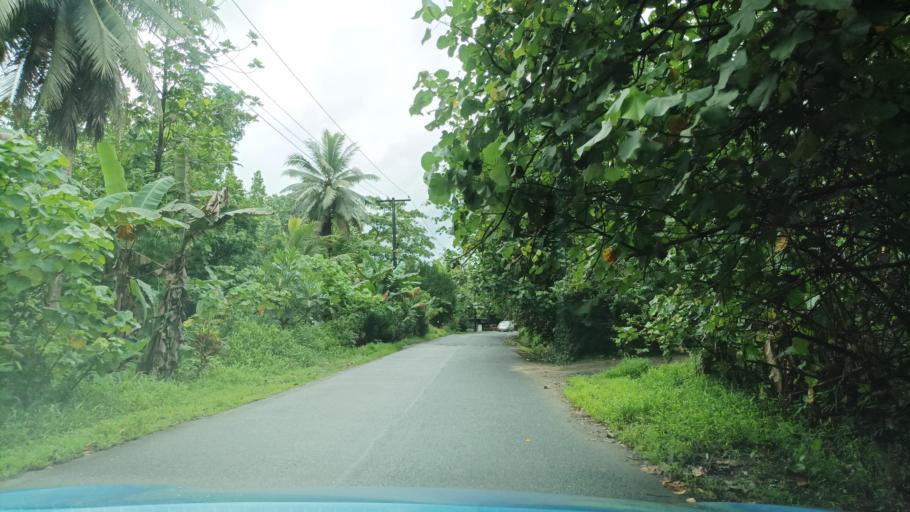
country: FM
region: Pohnpei
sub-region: Kolonia Municipality
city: Kolonia
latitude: 6.9372
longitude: 158.2786
